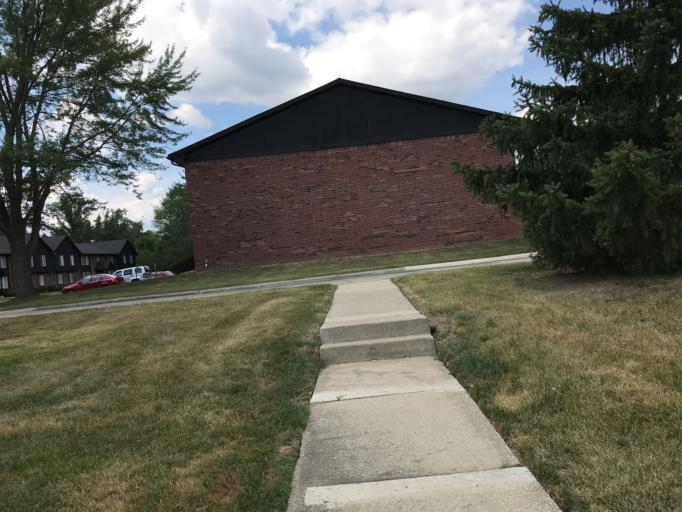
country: US
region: Michigan
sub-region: Oakland County
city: Bingham Farms
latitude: 42.5029
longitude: -83.2887
